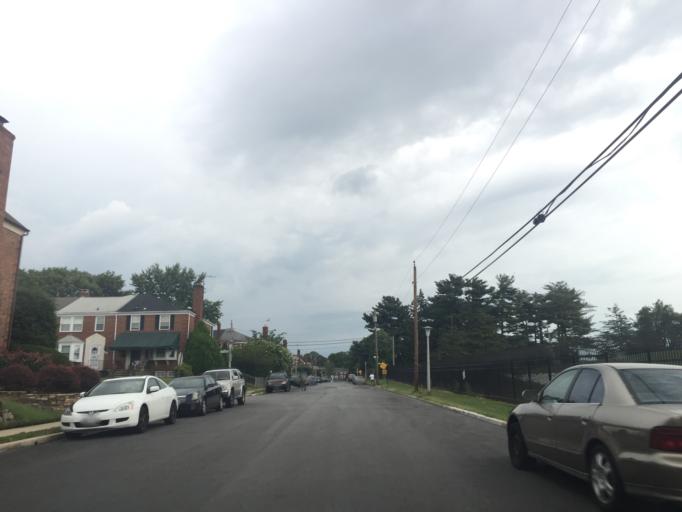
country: US
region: Maryland
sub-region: City of Baltimore
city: Baltimore
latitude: 39.3342
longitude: -76.5921
